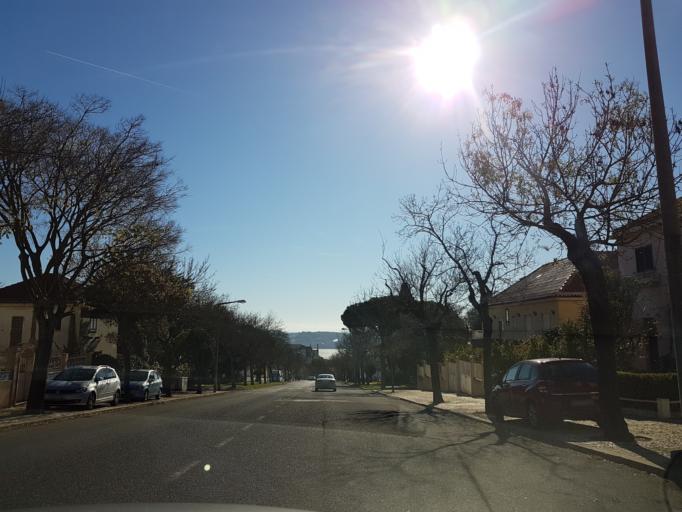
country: PT
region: Lisbon
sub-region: Oeiras
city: Alges
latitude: 38.7107
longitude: -9.2007
